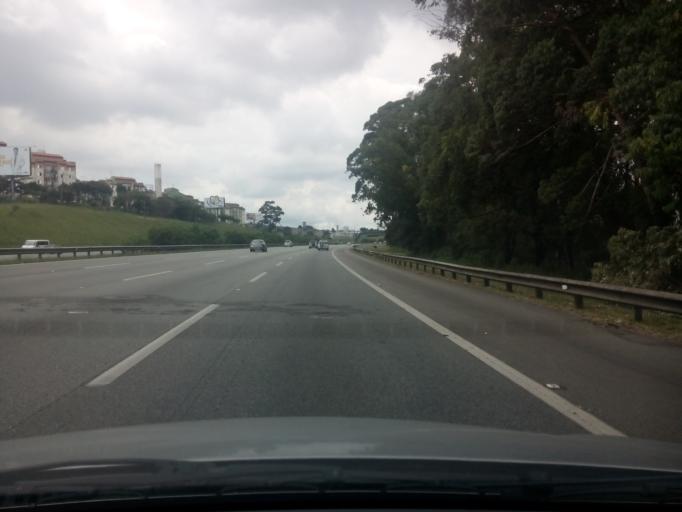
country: BR
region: Sao Paulo
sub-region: Diadema
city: Diadema
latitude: -23.6986
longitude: -46.6025
